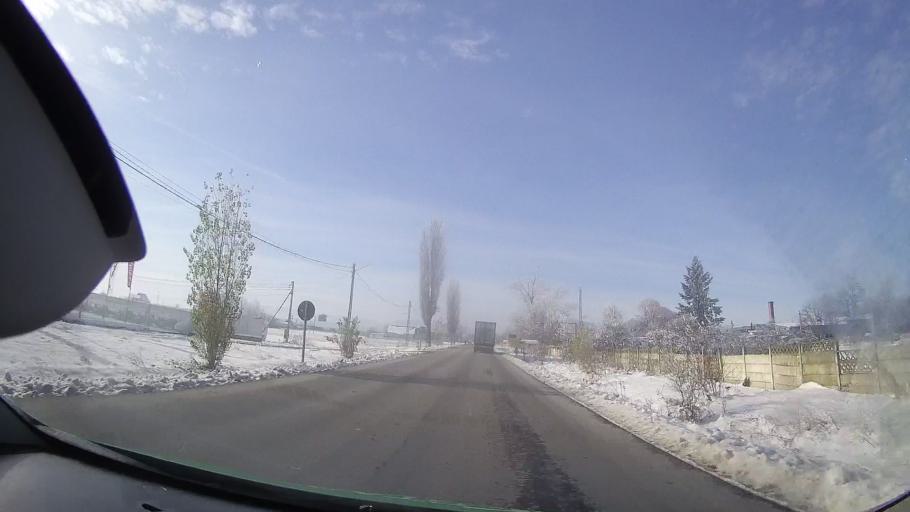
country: RO
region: Neamt
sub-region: Oras Targu Neamt
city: Targu Neamt
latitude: 47.2092
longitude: 26.4046
